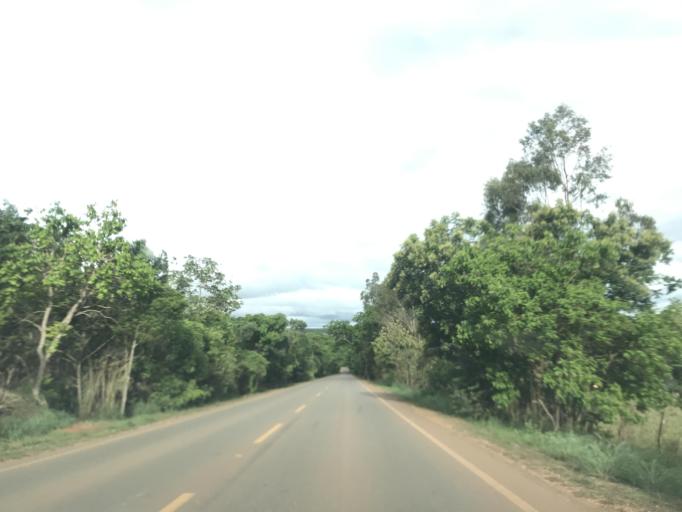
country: BR
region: Goias
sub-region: Vianopolis
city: Vianopolis
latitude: -16.5781
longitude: -48.3371
